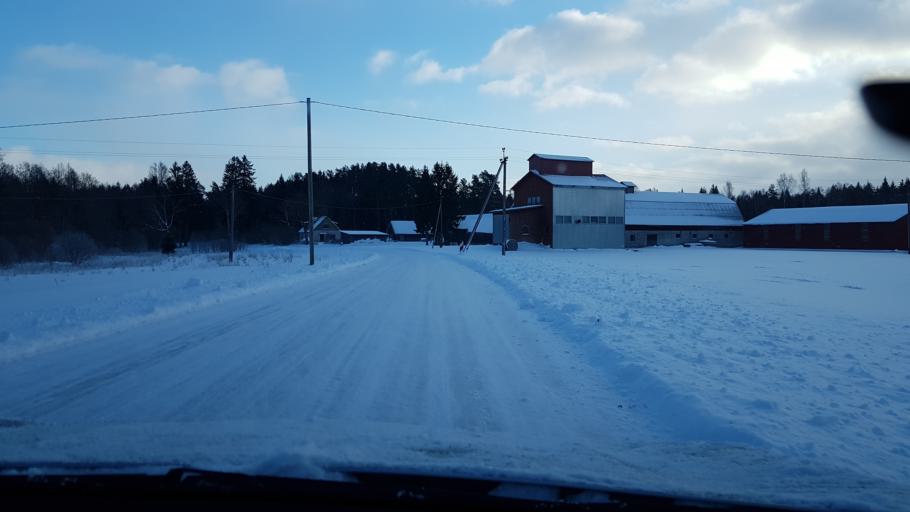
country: EE
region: Harju
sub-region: Nissi vald
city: Turba
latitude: 59.1397
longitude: 24.1667
